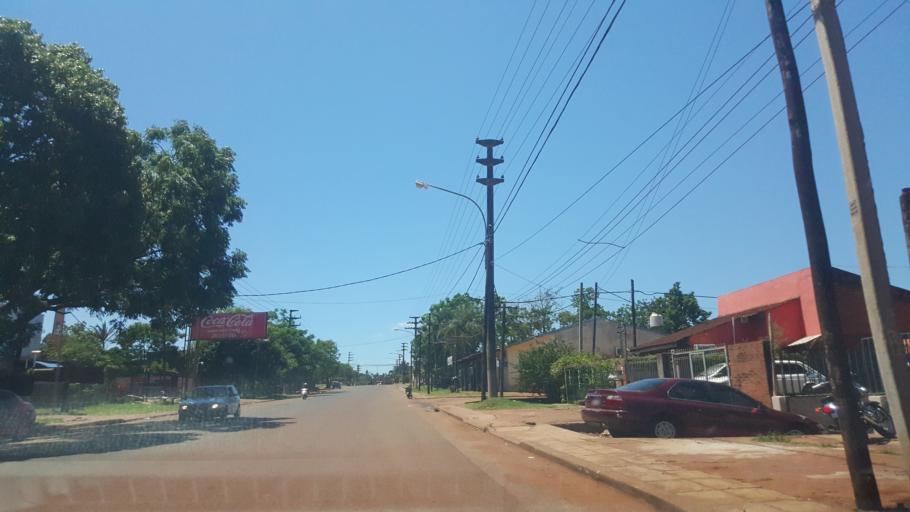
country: AR
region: Misiones
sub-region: Departamento de Capital
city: Posadas
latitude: -27.4068
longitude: -55.9114
